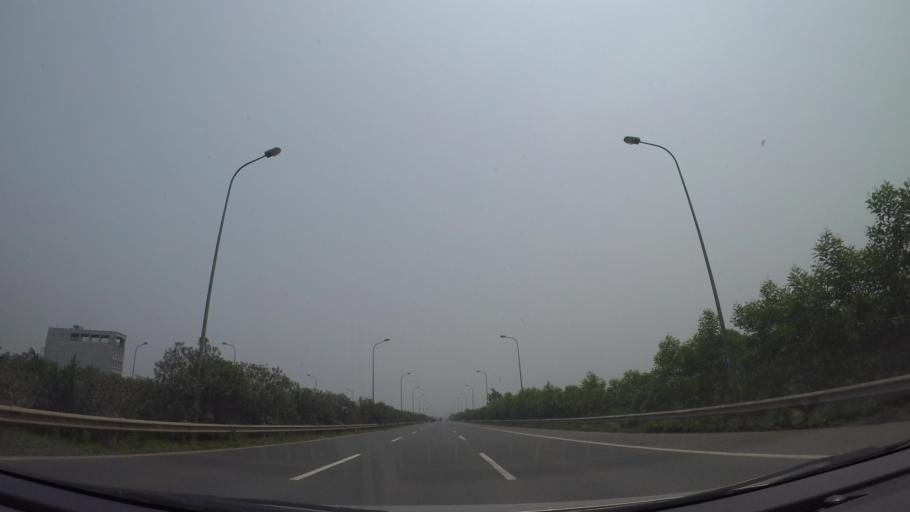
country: VN
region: Ha Noi
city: Quoc Oai
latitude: 20.9928
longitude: 105.5853
